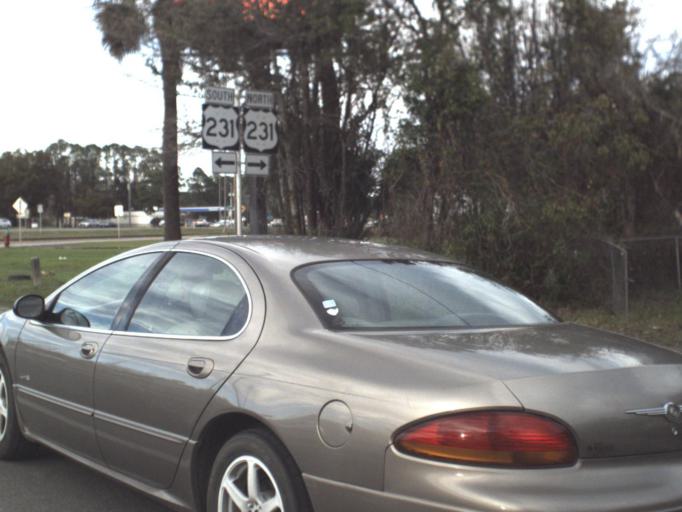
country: US
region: Florida
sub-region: Bay County
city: Hiland Park
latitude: 30.1999
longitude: -85.6249
